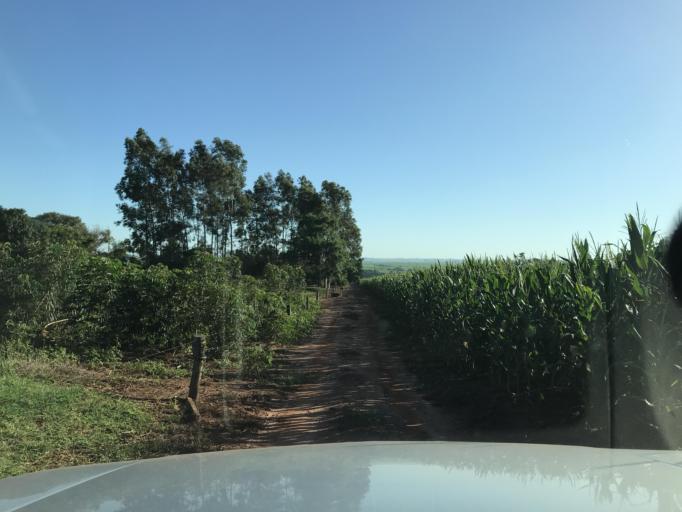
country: BR
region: Parana
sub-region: Palotina
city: Palotina
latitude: -24.2115
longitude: -53.7584
